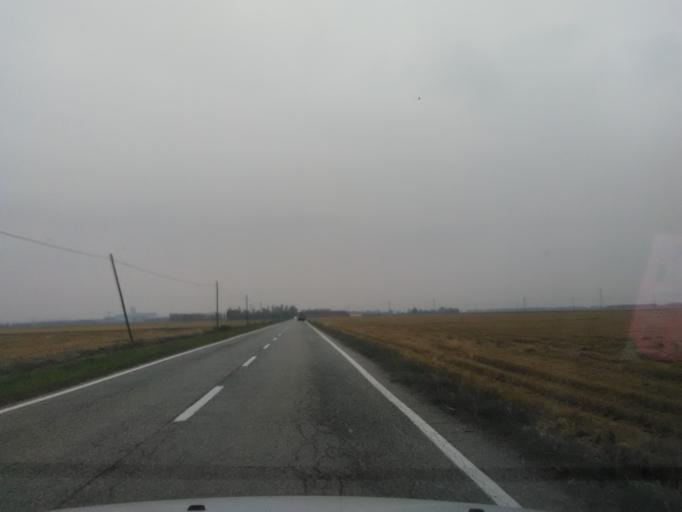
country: IT
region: Piedmont
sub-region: Provincia di Vercelli
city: Fontanetto Po
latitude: 45.2516
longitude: 8.1709
